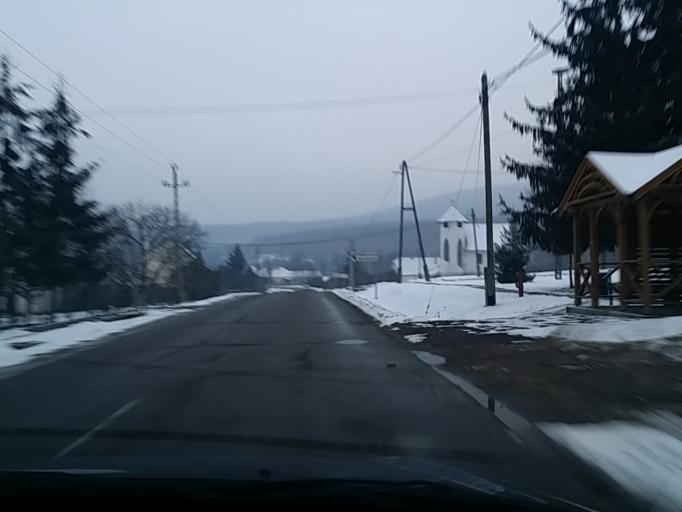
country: HU
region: Heves
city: Sirok
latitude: 47.9012
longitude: 20.1792
